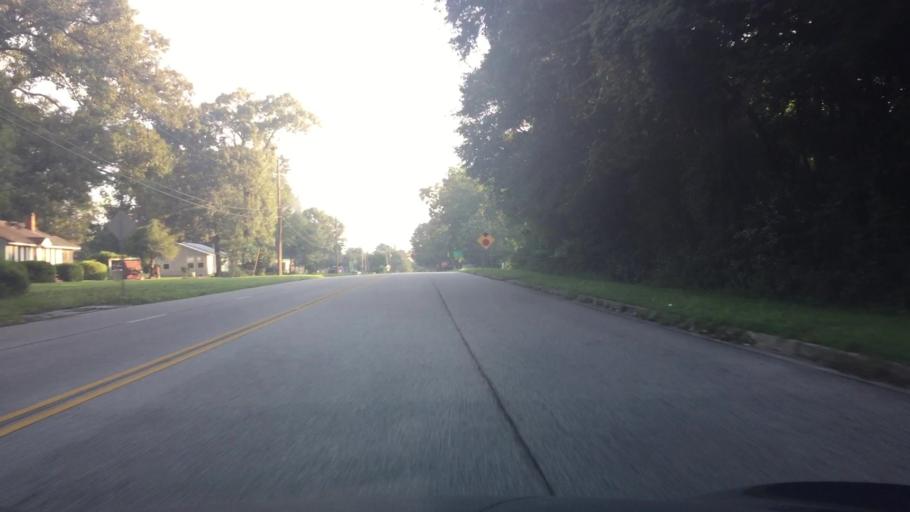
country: US
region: Alabama
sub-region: Covington County
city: Florala
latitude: 30.9970
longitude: -86.3089
